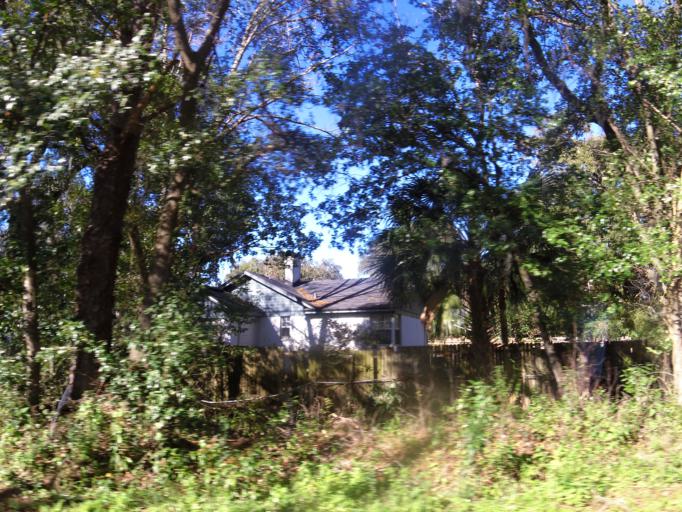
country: US
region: Florida
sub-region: Duval County
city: Jacksonville
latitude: 30.2820
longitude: -81.6492
